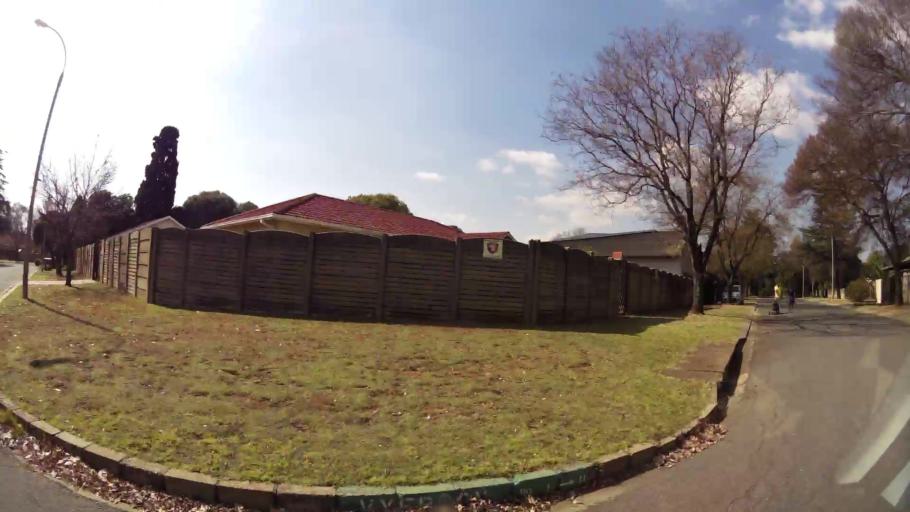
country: ZA
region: Gauteng
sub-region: City of Johannesburg Metropolitan Municipality
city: Modderfontein
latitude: -26.0809
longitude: 28.2308
